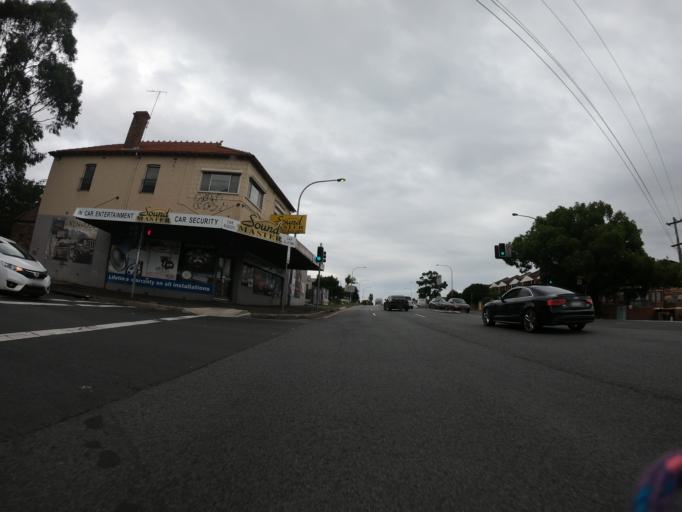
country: AU
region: New South Wales
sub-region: Parramatta
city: Harris Park
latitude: -33.8347
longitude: 151.0021
